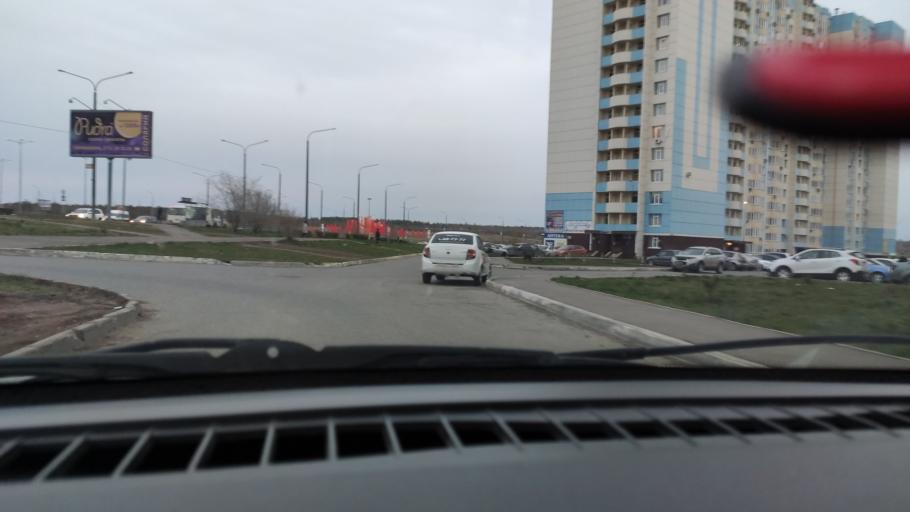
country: RU
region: Orenburg
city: Orenburg
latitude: 51.8117
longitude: 55.1776
